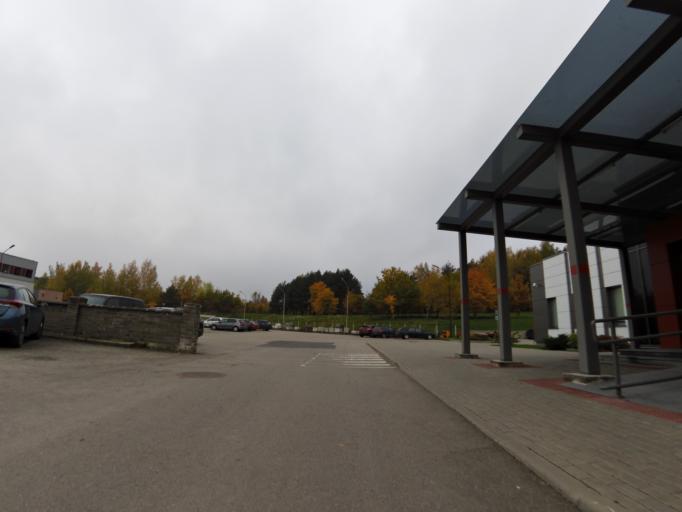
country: LT
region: Vilnius County
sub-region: Vilnius
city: Fabijoniskes
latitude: 54.7535
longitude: 25.2769
